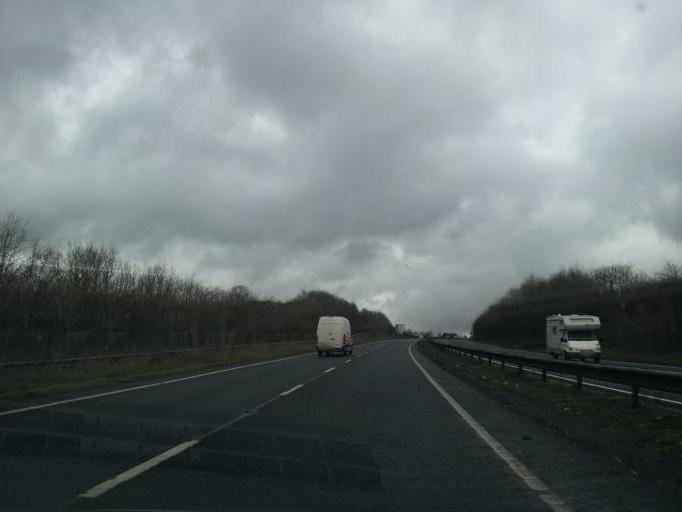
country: GB
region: England
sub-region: Somerset
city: Wincanton
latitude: 51.0675
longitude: -2.3648
